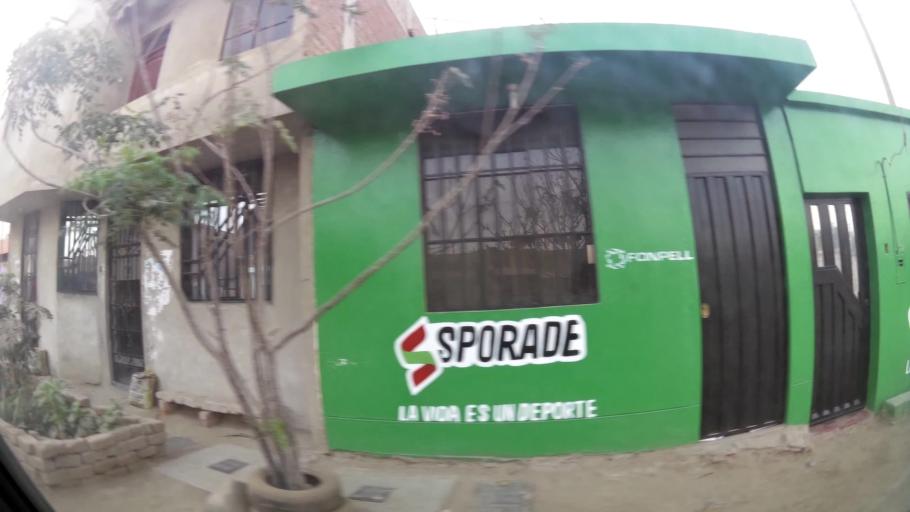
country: PE
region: La Libertad
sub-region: Provincia de Trujillo
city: El Porvenir
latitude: -8.0654
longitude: -79.0111
